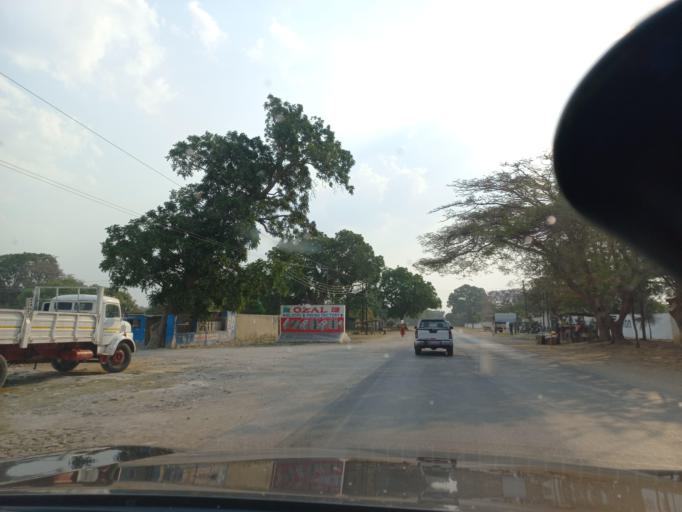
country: ZM
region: Lusaka
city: Lusaka
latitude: -15.4651
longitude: 28.2322
